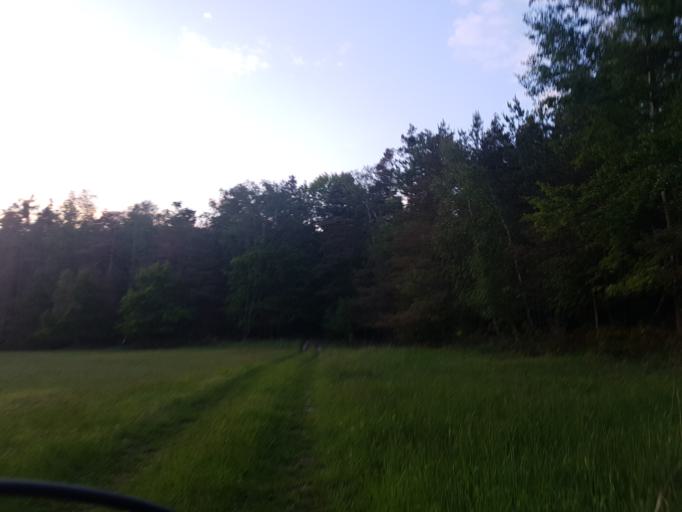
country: DE
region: Brandenburg
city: Trobitz
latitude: 51.5775
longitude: 13.4168
